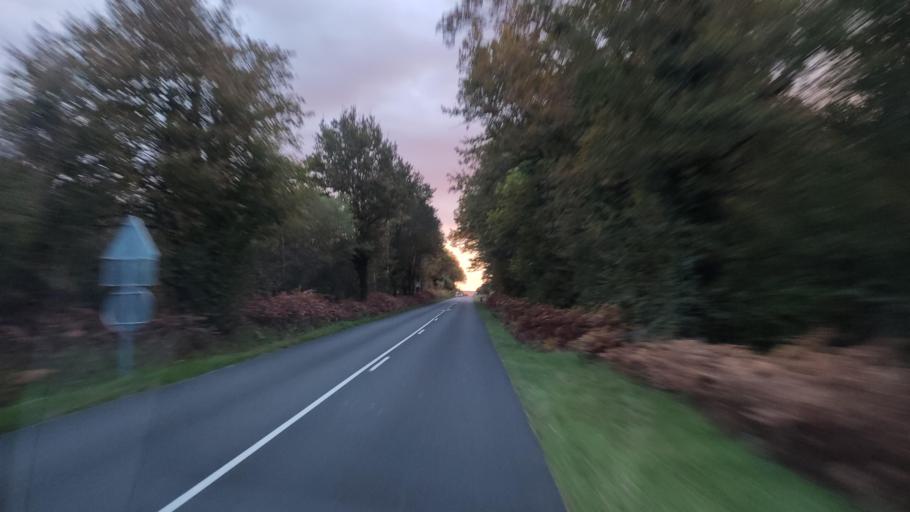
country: FR
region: Limousin
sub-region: Departement de la Haute-Vienne
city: Rilhac-Rancon
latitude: 45.9165
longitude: 1.3369
